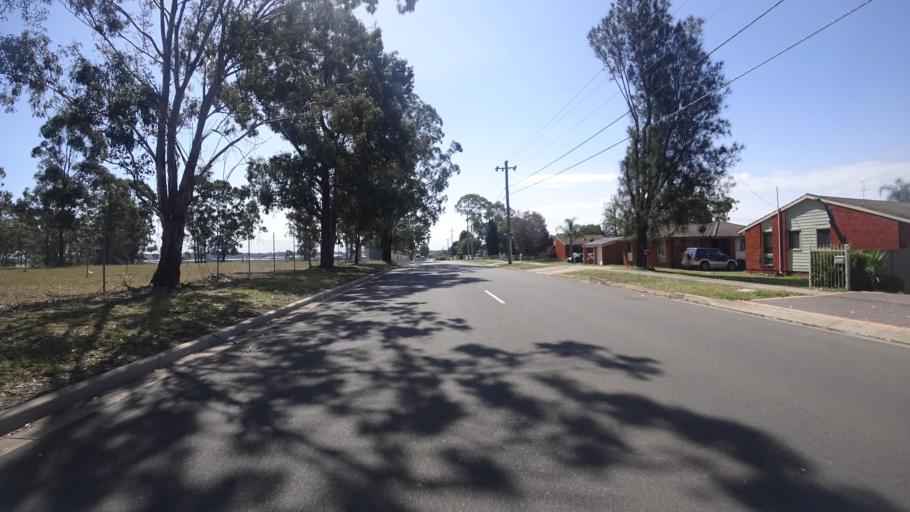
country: AU
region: New South Wales
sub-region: Liverpool
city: Miller
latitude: -33.9423
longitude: 150.8887
